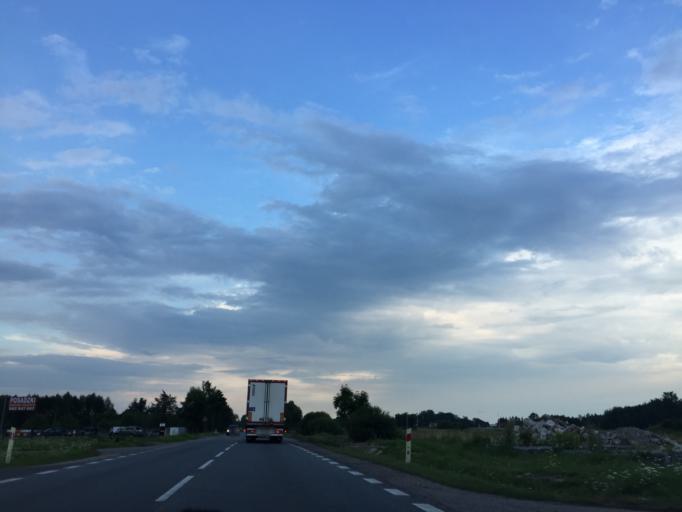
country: PL
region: Masovian Voivodeship
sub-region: Powiat minski
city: Minsk Mazowiecki
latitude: 52.2135
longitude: 21.5381
